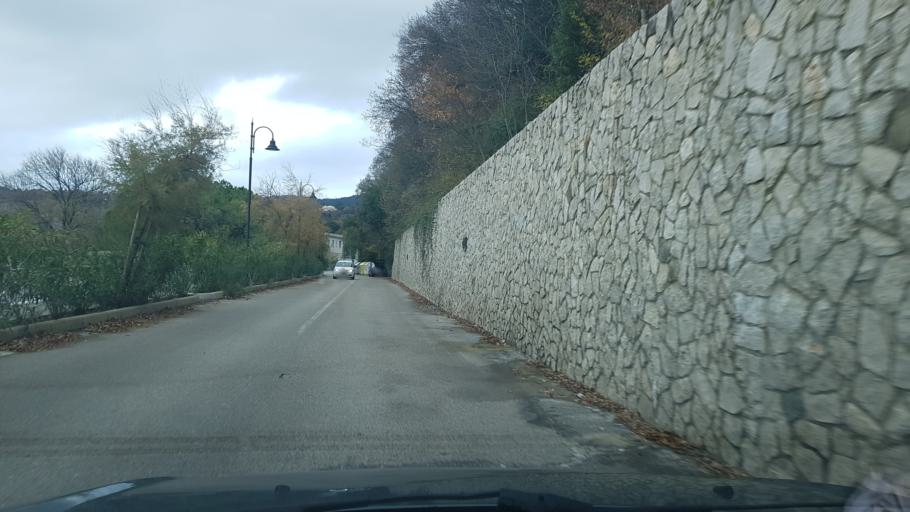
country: IT
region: Friuli Venezia Giulia
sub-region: Provincia di Trieste
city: Sistiana-Visogliano
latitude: 45.7663
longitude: 13.6339
